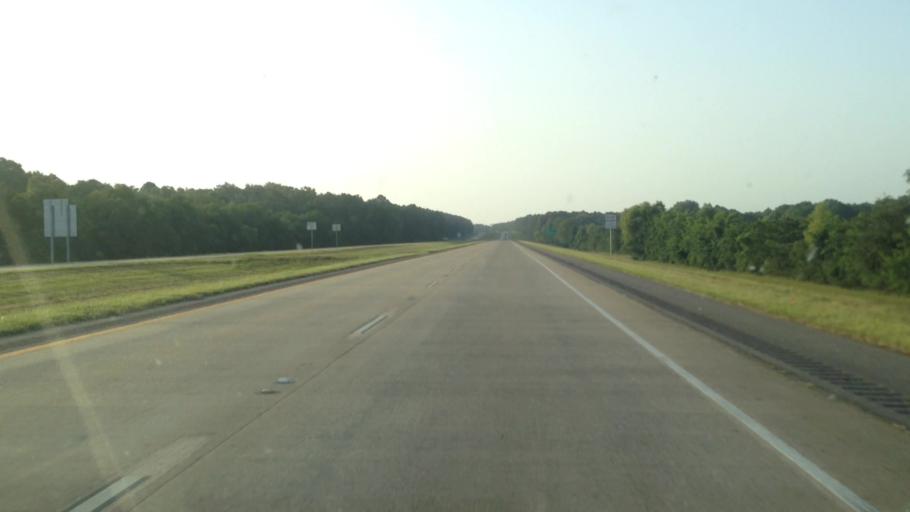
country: US
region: Louisiana
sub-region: Grant Parish
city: Colfax
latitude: 31.4859
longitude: -92.8502
